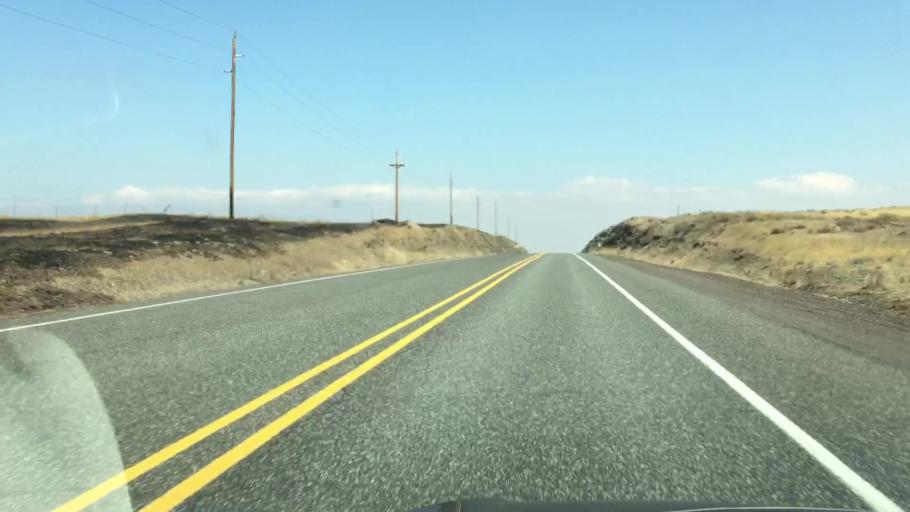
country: US
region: Oregon
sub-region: Wasco County
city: The Dalles
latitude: 45.3572
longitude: -121.1421
